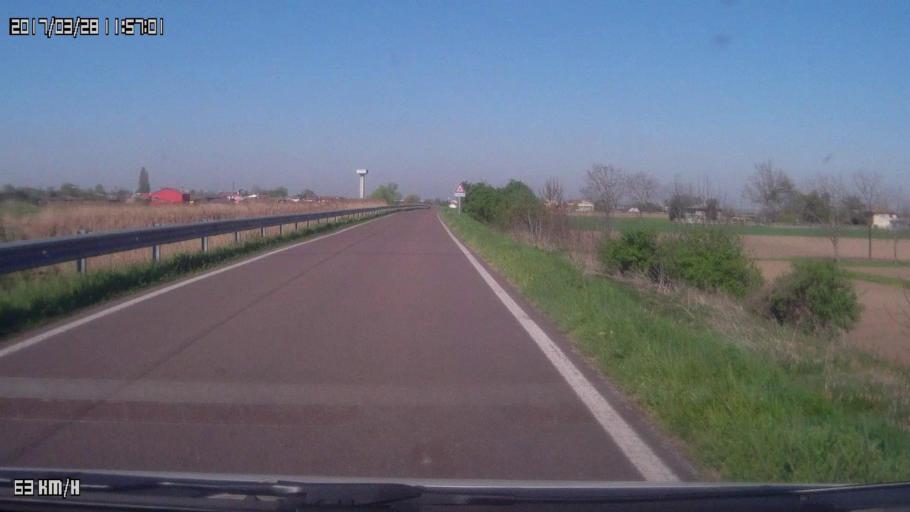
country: IT
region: Veneto
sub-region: Provincia di Venezia
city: Boscochiaro
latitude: 45.1352
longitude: 12.1312
